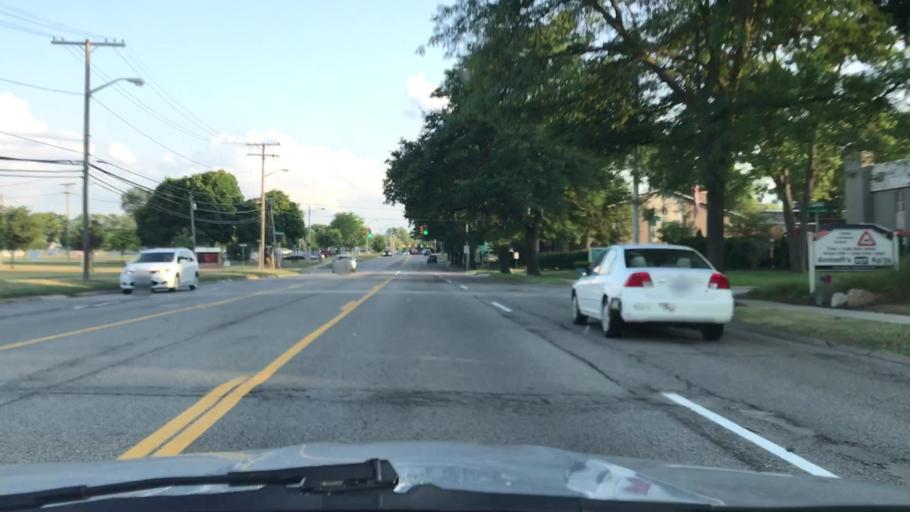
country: US
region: Michigan
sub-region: Oakland County
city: Clawson
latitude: 42.5226
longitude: -83.1651
